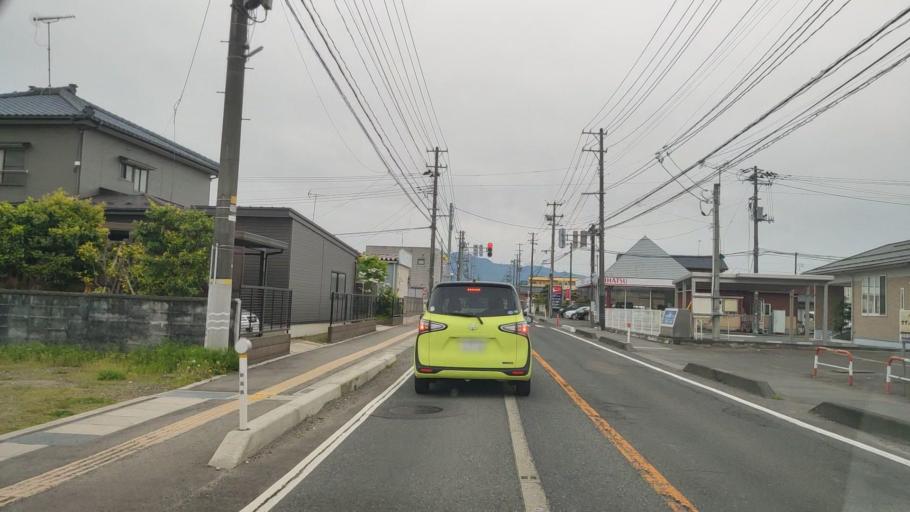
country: JP
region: Niigata
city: Gosen
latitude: 37.7318
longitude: 139.1769
